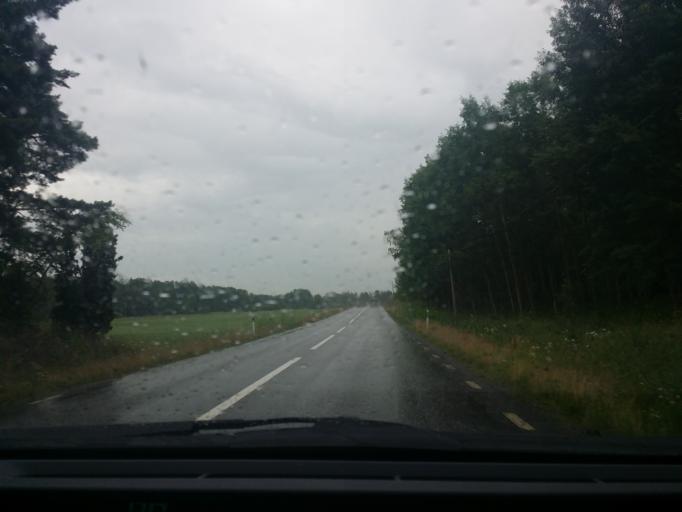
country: SE
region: OErebro
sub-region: Lindesbergs Kommun
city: Fellingsbro
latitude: 59.4262
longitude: 15.6204
